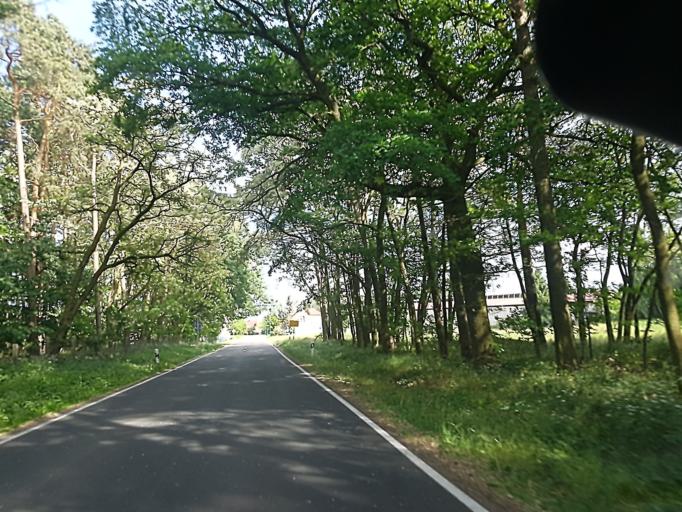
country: DE
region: Saxony-Anhalt
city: Kropstadt
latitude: 51.9681
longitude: 12.7398
